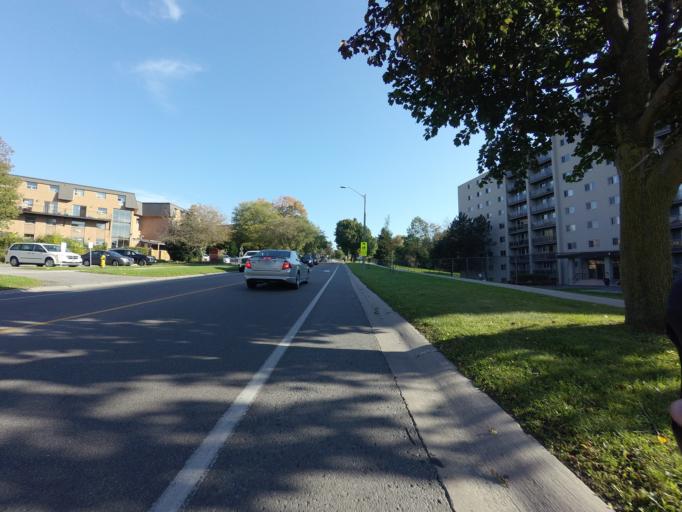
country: CA
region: Ontario
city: Kingston
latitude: 44.2356
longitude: -76.5346
